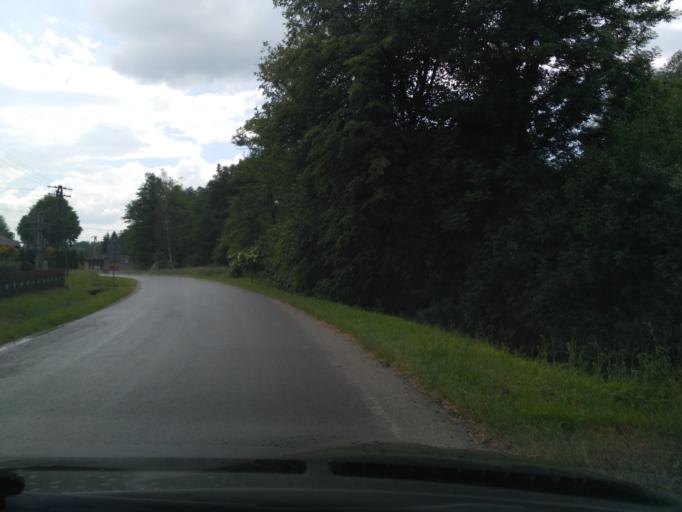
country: PL
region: Subcarpathian Voivodeship
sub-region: Powiat lancucki
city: Husow
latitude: 49.9497
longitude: 22.2790
